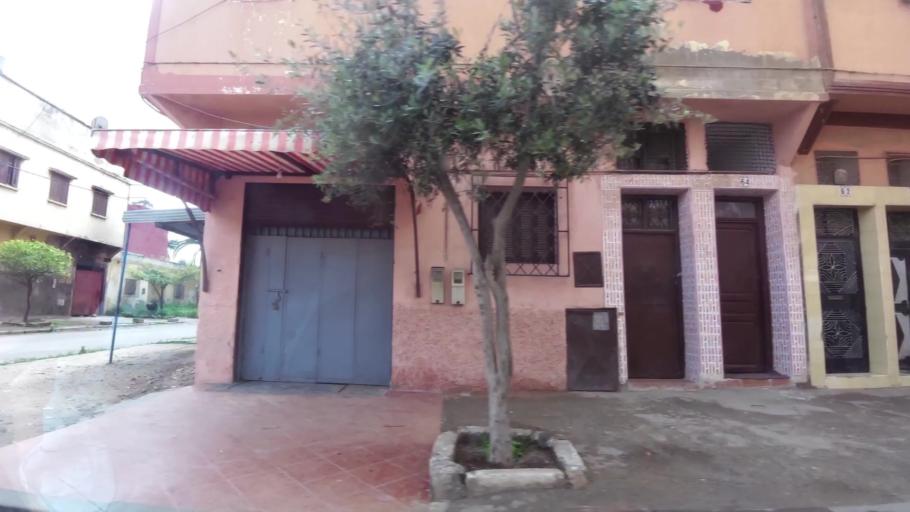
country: MA
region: Chaouia-Ouardigha
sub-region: Settat Province
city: Berrechid
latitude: 33.2691
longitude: -7.5880
